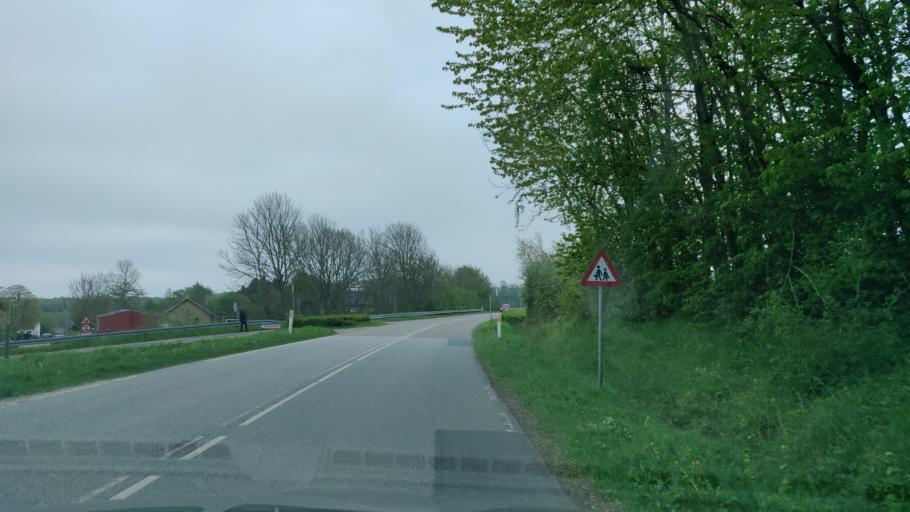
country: DK
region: South Denmark
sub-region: Sonderborg Kommune
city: Guderup
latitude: 54.9998
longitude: 9.9515
